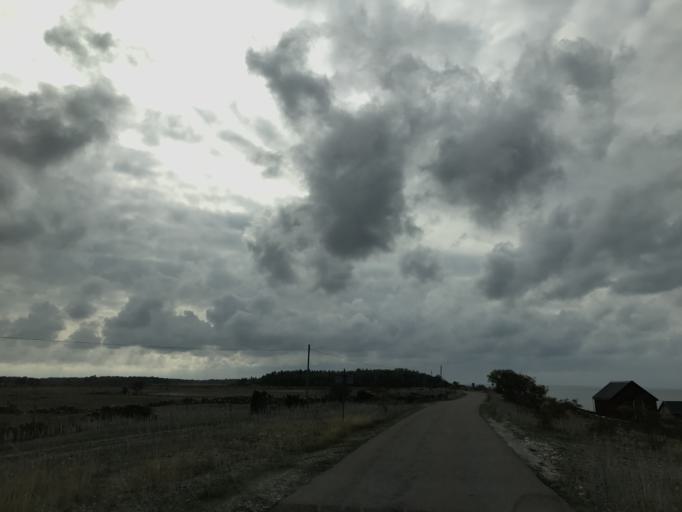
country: SE
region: Kalmar
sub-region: Borgholms Kommun
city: Borgholm
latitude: 57.0652
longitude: 16.8439
